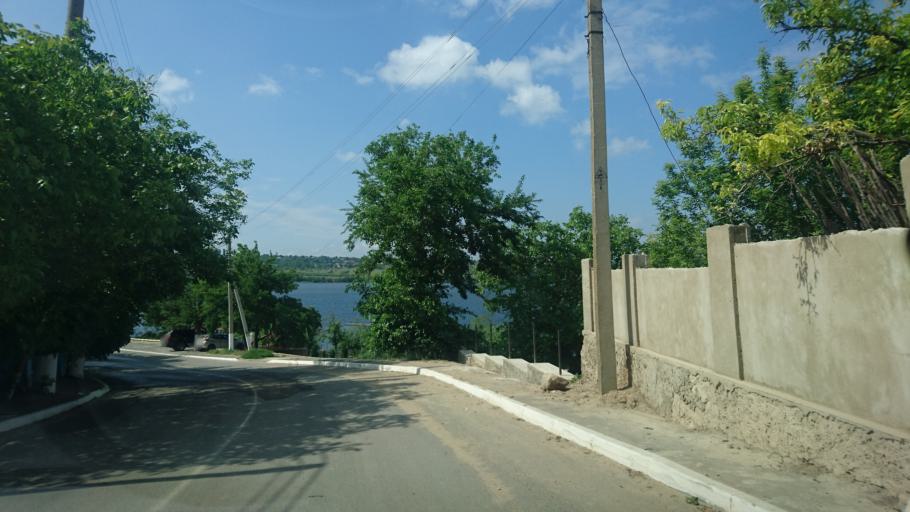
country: MD
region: Telenesti
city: Cocieri
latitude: 47.3549
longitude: 29.1061
